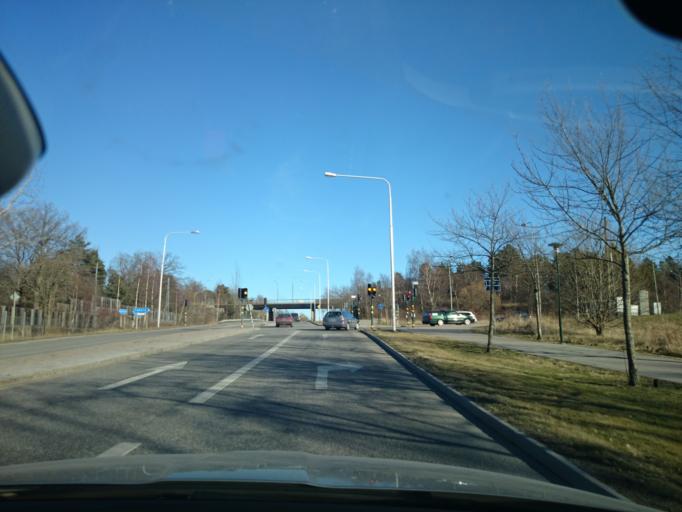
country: SE
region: Stockholm
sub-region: Stockholms Kommun
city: Arsta
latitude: 59.2430
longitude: 18.0766
